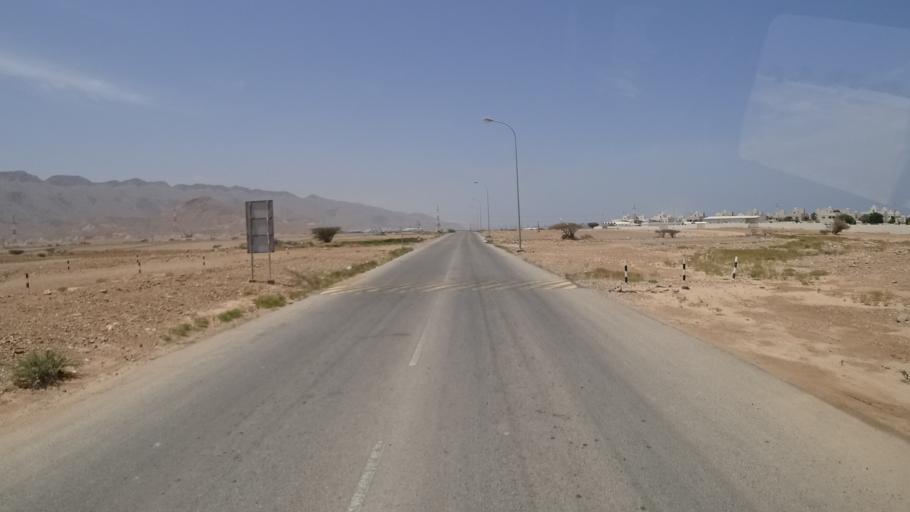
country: OM
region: Ash Sharqiyah
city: Sur
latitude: 22.6028
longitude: 59.4373
